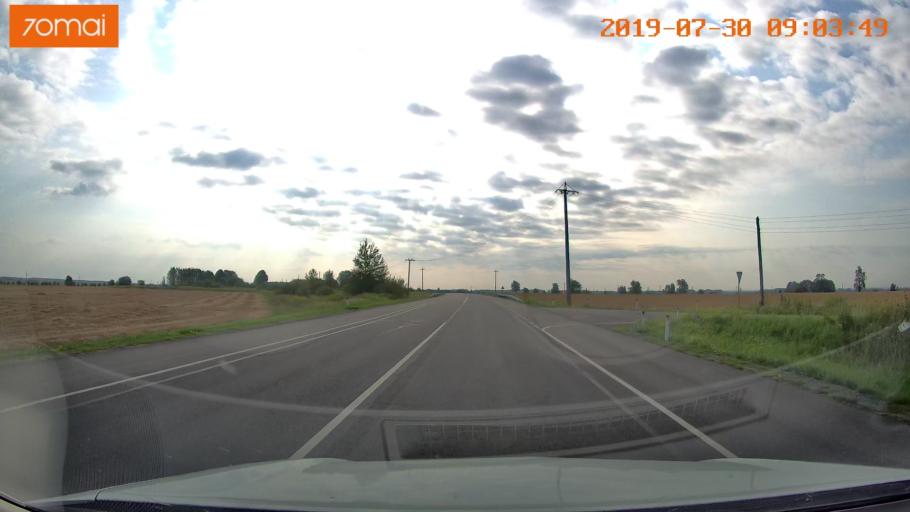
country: RU
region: Kaliningrad
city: Gusev
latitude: 54.6058
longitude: 22.2635
